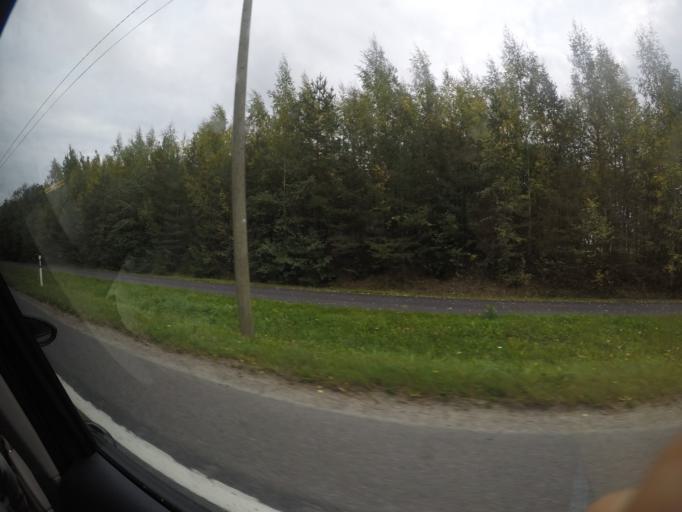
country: FI
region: Haeme
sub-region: Haemeenlinna
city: Haemeenlinna
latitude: 61.0239
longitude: 24.4222
